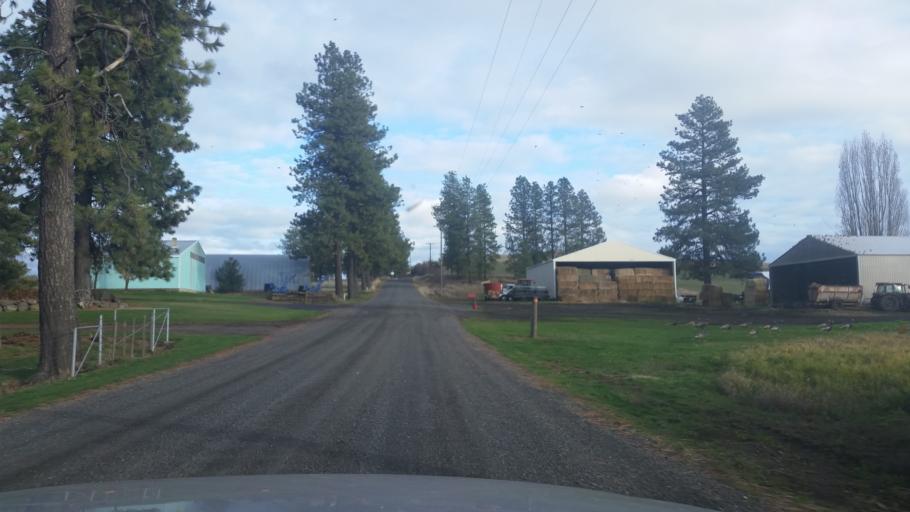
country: US
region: Washington
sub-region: Spokane County
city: Cheney
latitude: 47.4272
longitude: -117.4316
